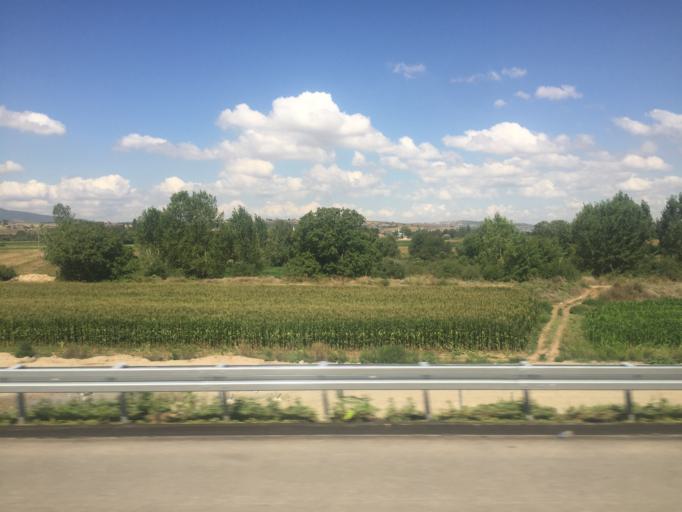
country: TR
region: Balikesir
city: Gobel
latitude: 39.9910
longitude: 28.1883
